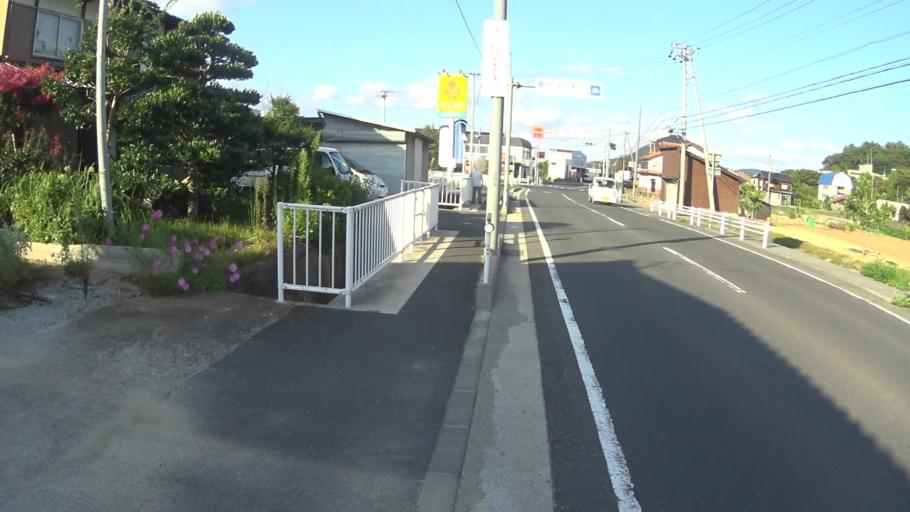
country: JP
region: Kyoto
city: Miyazu
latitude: 35.7677
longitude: 135.2306
